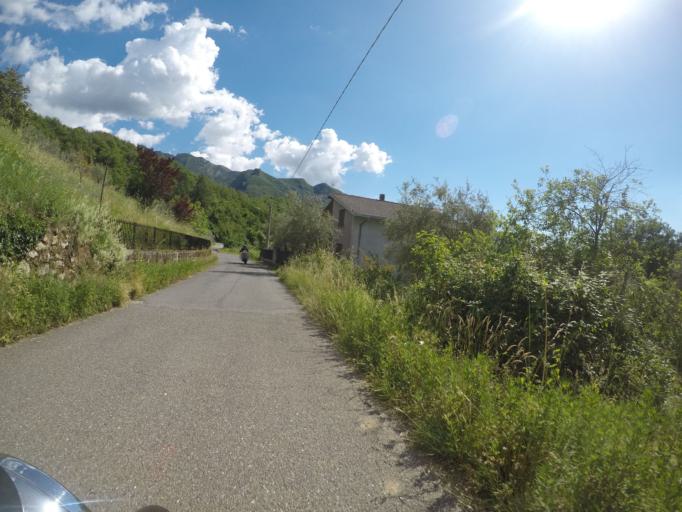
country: IT
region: Tuscany
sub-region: Provincia di Massa-Carrara
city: Casola in Lunigiana
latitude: 44.1788
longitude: 10.1521
